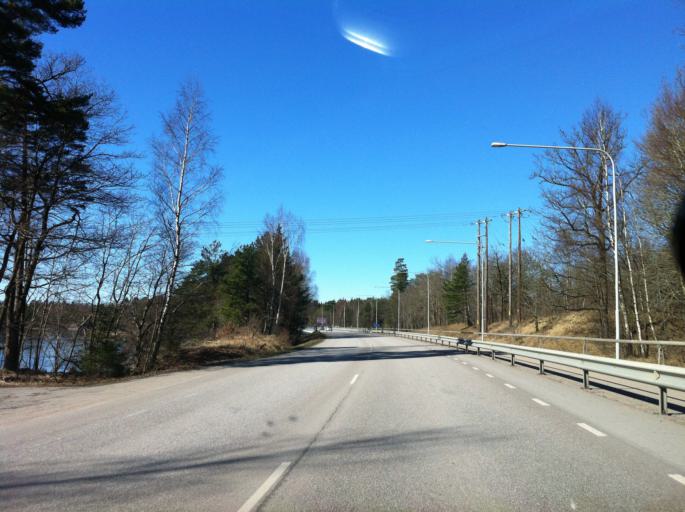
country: SE
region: Vaestra Goetaland
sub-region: Vanersborgs Kommun
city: Vargon
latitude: 58.3580
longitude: 12.4264
